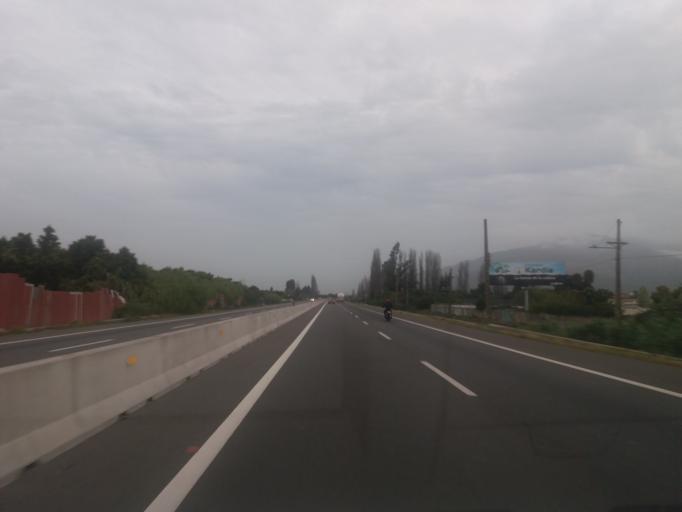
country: CL
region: Valparaiso
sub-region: Provincia de Quillota
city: Hacienda La Calera
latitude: -32.8066
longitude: -71.2190
